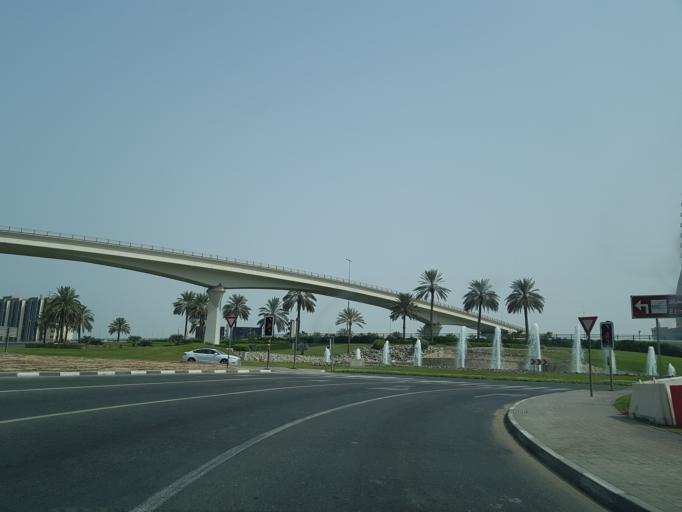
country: AE
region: Ash Shariqah
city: Sharjah
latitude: 25.2284
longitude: 55.2900
